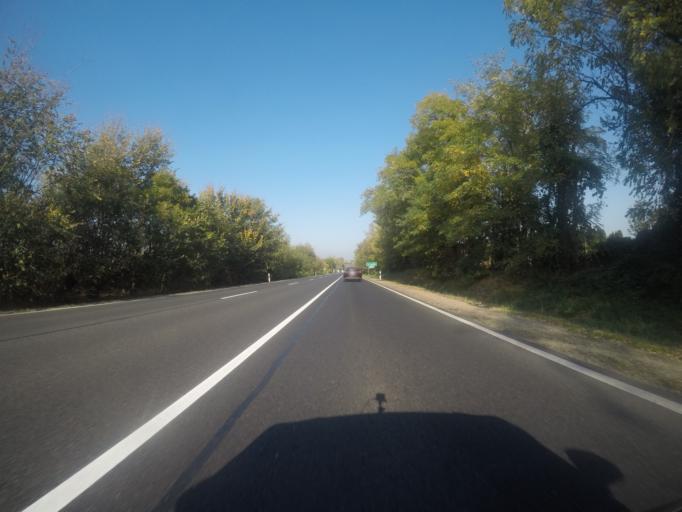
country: HU
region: Fejer
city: Baracs
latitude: 46.8620
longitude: 18.9156
